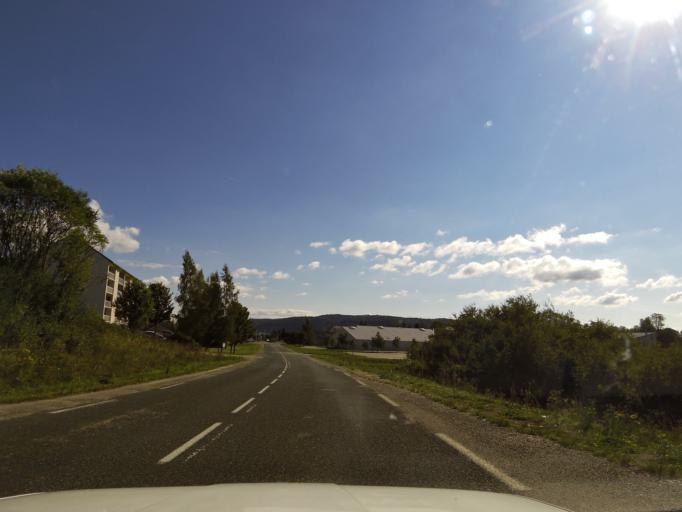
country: FR
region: Rhone-Alpes
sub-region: Departement de l'Ain
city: Hauteville-Lompnes
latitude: 45.9827
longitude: 5.5976
